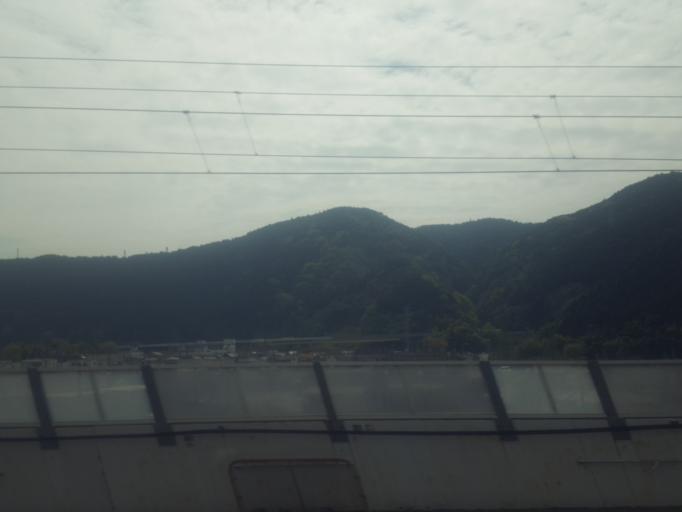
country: JP
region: Yamaguchi
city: Iwakuni
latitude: 34.1705
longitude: 132.1534
